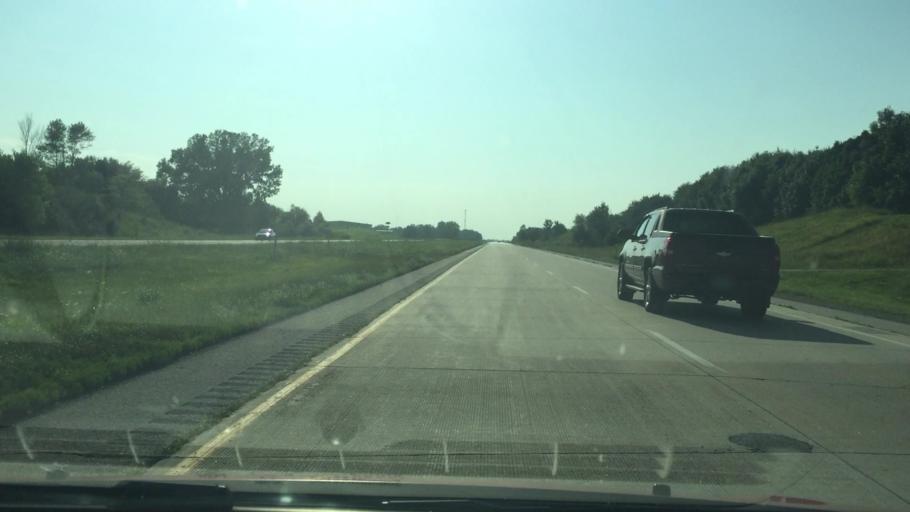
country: US
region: Iowa
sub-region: Scott County
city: Blue Grass
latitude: 41.5161
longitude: -90.8303
